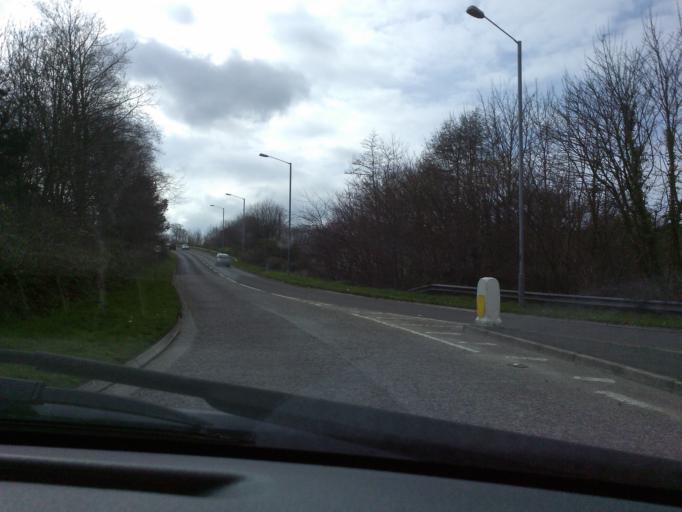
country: GB
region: England
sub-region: Cornwall
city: Penzance
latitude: 50.1294
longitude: -5.5423
